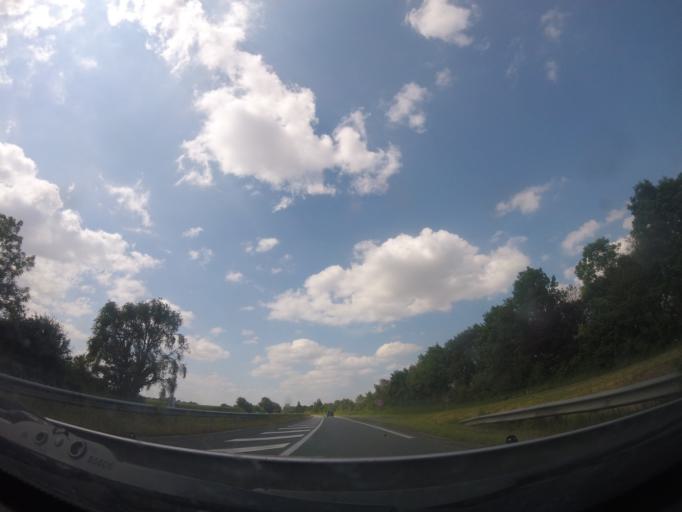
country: FR
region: Poitou-Charentes
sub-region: Departement de la Charente-Maritime
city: Saint-Porchaire
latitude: 45.8283
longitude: -0.7962
